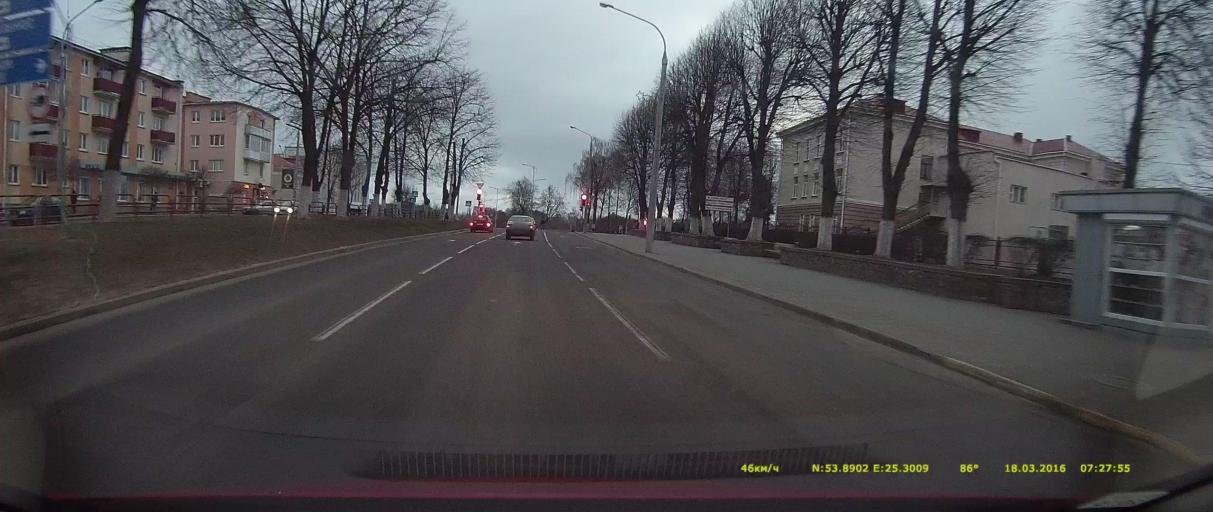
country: BY
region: Grodnenskaya
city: Lida
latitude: 53.8902
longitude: 25.3011
